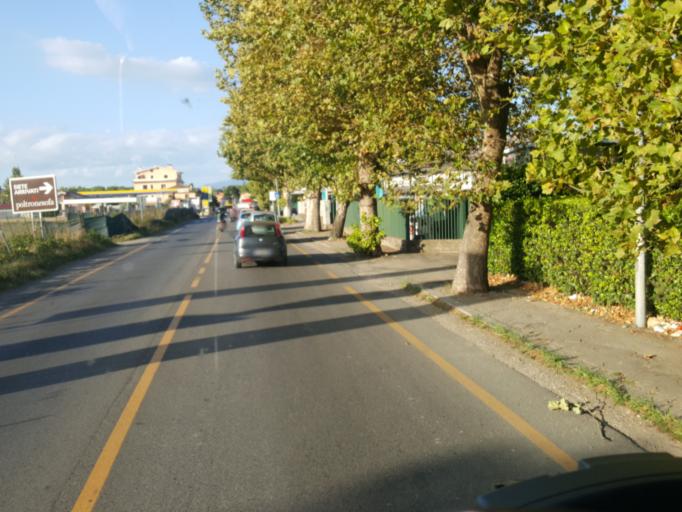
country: IT
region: Latium
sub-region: Citta metropolitana di Roma Capitale
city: Bivio di Capanelle
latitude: 42.1167
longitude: 12.5884
